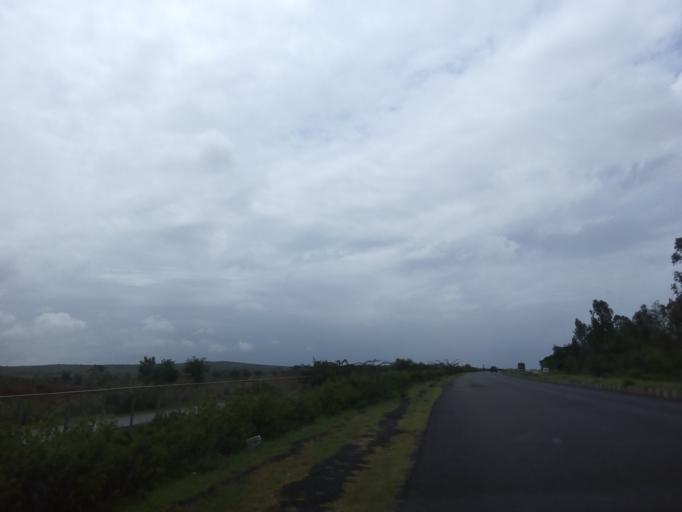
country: IN
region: Karnataka
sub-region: Haveri
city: Byadgi
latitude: 14.7100
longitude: 75.5097
